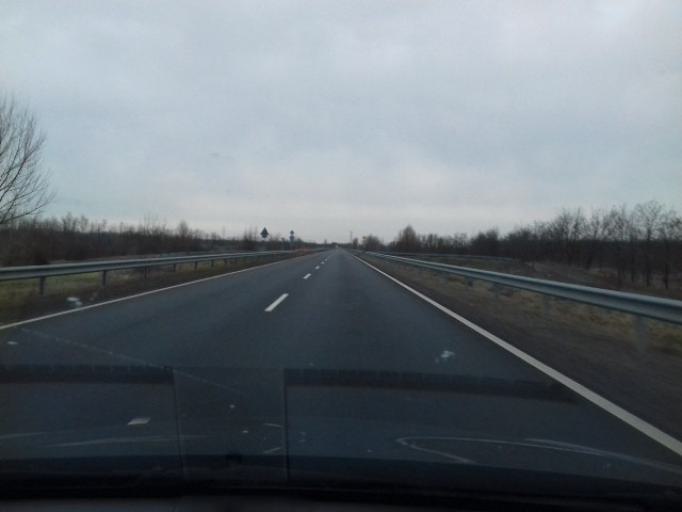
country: HU
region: Szabolcs-Szatmar-Bereg
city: Nyirpazony
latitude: 47.9709
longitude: 21.8170
